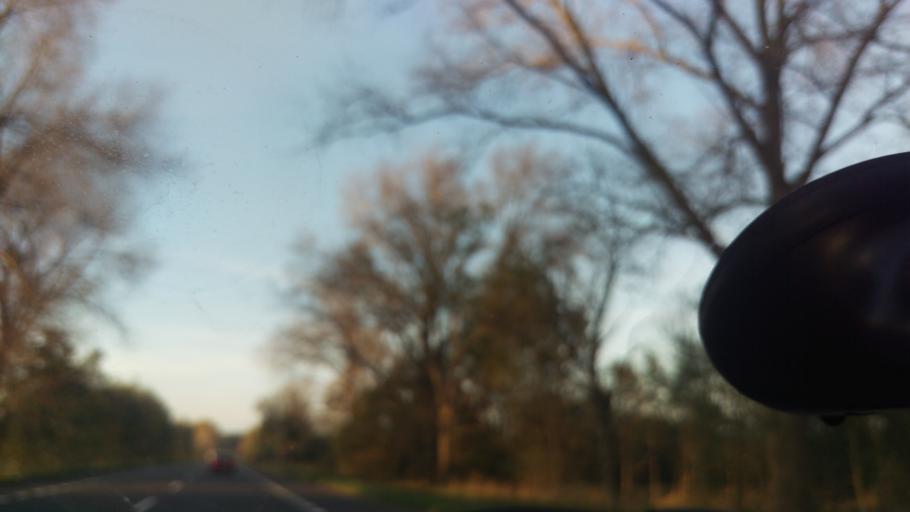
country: PL
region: West Pomeranian Voivodeship
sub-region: Powiat gryfinski
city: Stare Czarnowo
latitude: 53.2439
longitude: 14.7818
